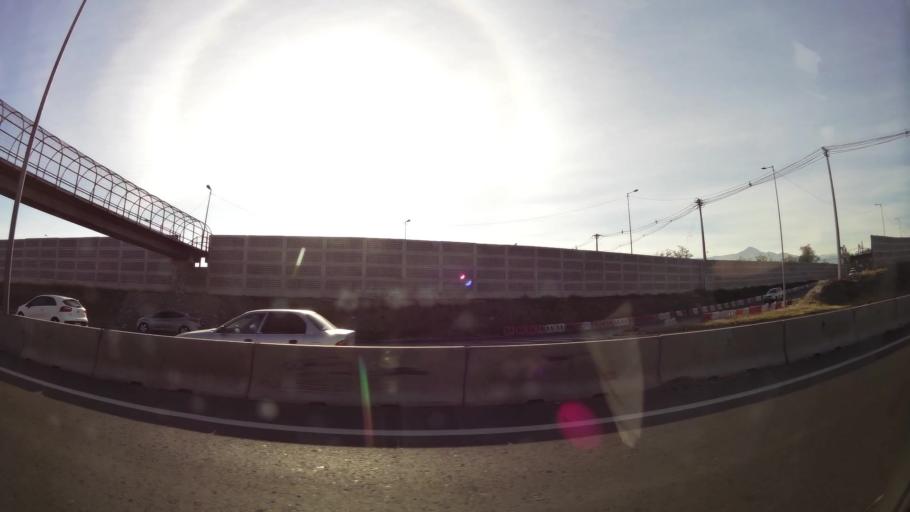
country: CL
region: Santiago Metropolitan
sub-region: Provincia de Santiago
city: La Pintana
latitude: -33.5810
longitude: -70.6111
